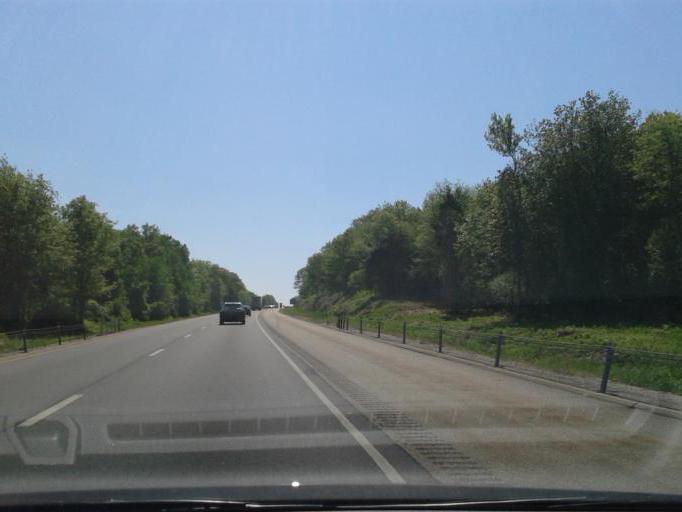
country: US
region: Connecticut
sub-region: New London County
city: Pawcatuck
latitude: 41.3908
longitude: -71.8773
